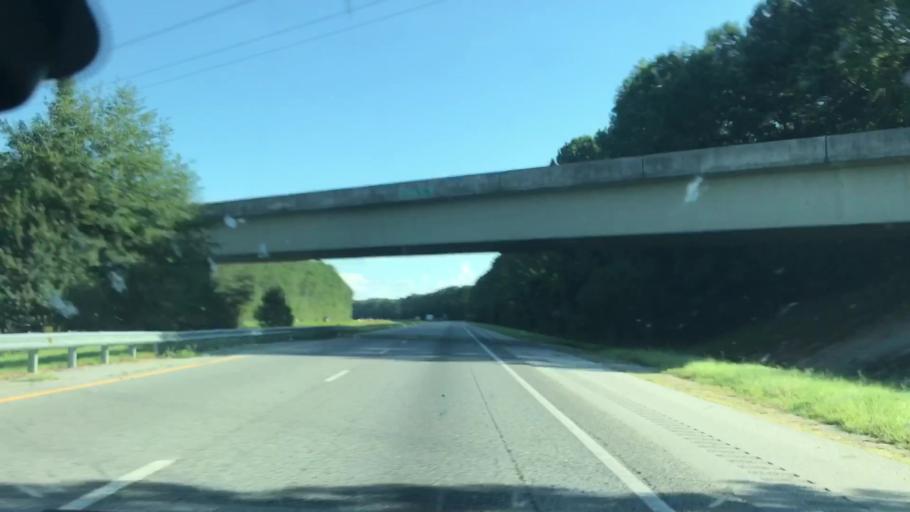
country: US
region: Georgia
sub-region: Harris County
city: Hamilton
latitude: 32.6793
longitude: -84.9897
